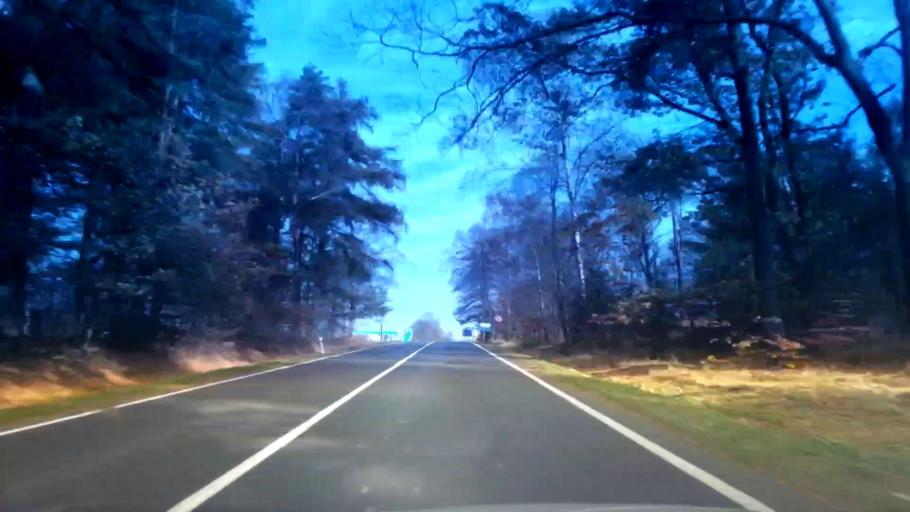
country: CZ
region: Karlovarsky
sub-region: Okres Cheb
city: Cheb
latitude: 50.0454
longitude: 12.3483
